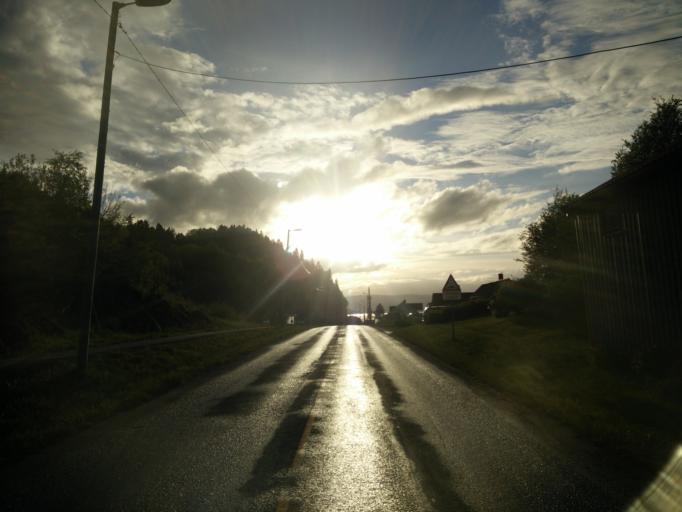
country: NO
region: Sor-Trondelag
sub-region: Skaun
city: Borsa
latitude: 63.3196
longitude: 10.1426
